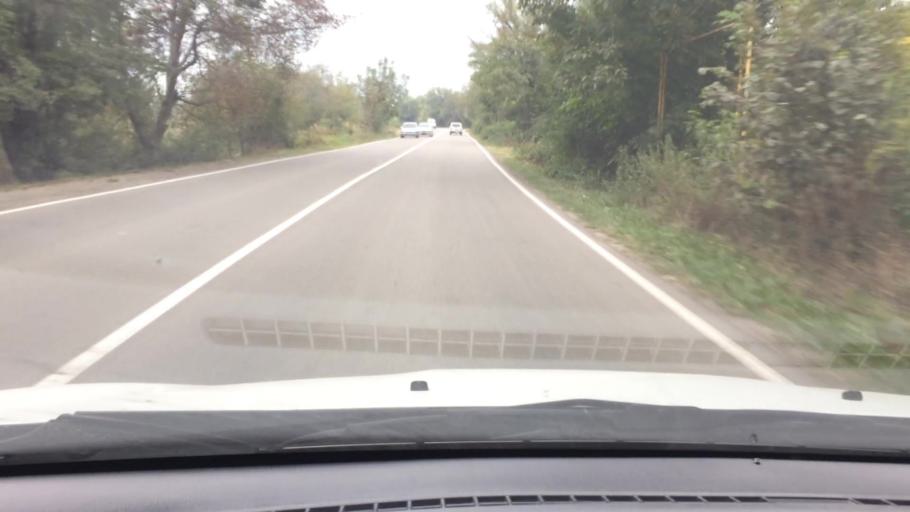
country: AM
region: Tavush
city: Bagratashen
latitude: 41.2608
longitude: 44.7961
